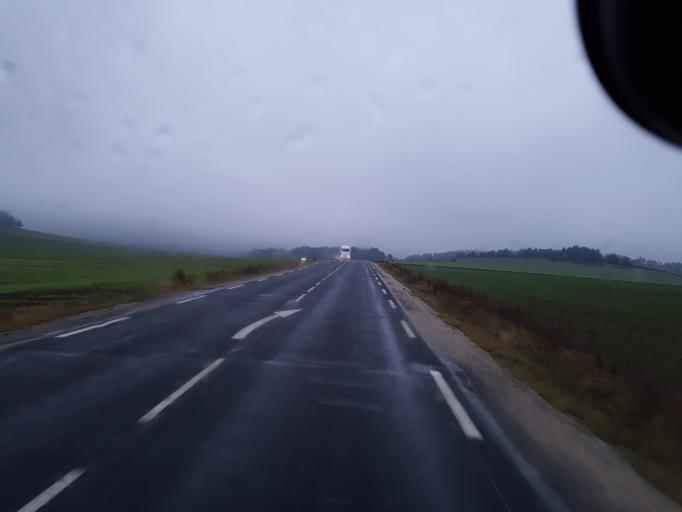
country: FR
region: Languedoc-Roussillon
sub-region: Departement de la Lozere
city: Langogne
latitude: 44.8346
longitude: 3.8613
